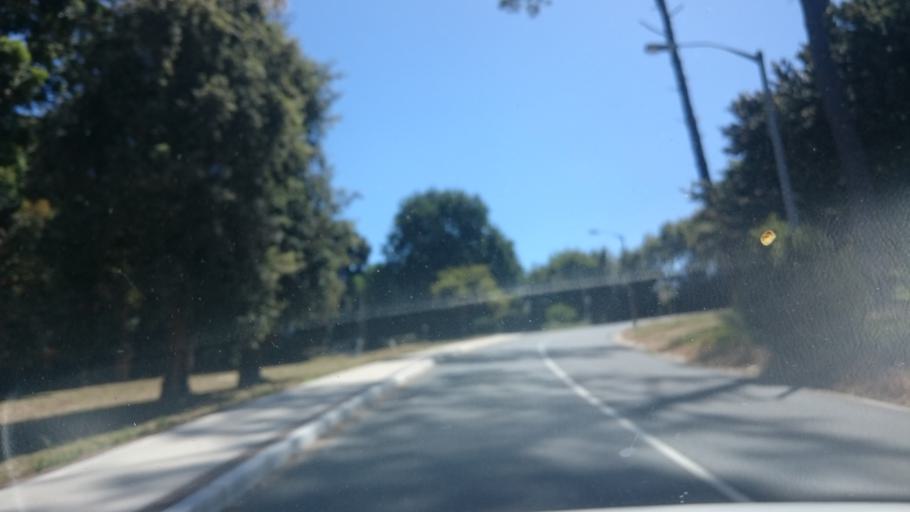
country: ZA
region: Western Cape
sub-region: City of Cape Town
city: Newlands
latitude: -34.0002
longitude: 18.4498
